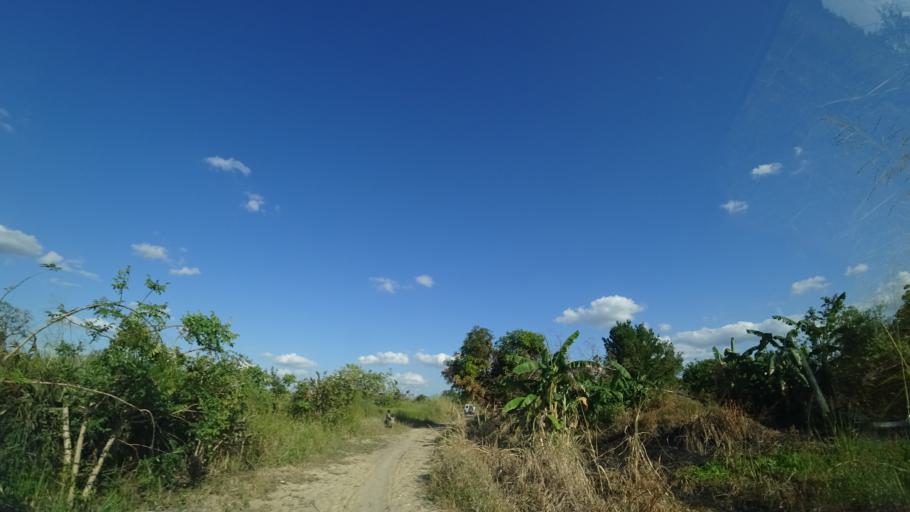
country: MZ
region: Sofala
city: Dondo
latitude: -19.3487
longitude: 34.5839
